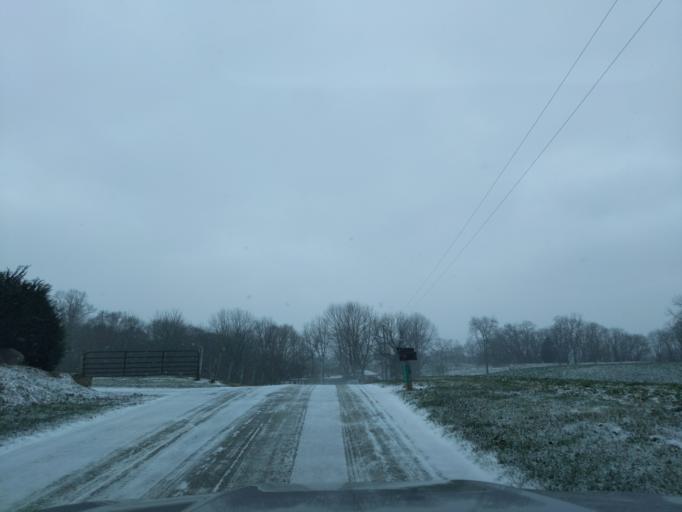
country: US
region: Indiana
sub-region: Decatur County
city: Westport
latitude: 39.2285
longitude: -85.5105
